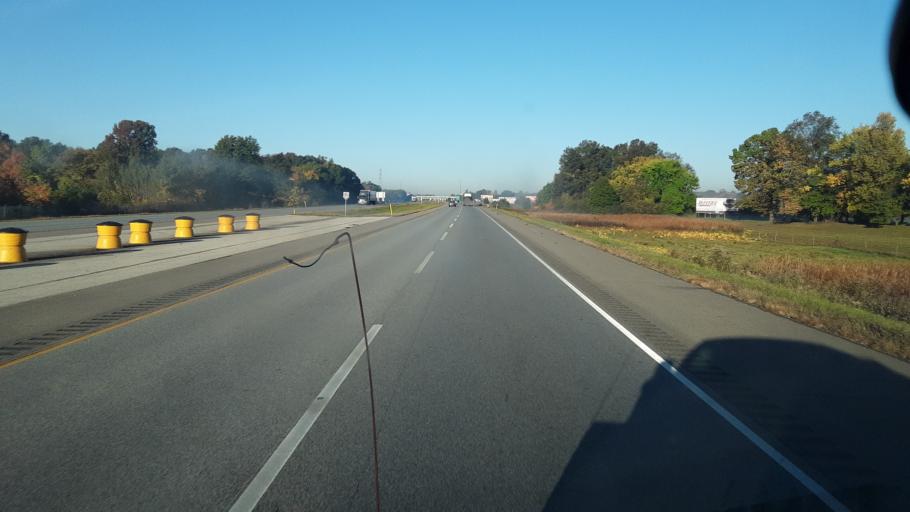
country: US
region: Indiana
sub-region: Elkhart County
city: Simonton Lake
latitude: 41.7312
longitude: -85.9516
